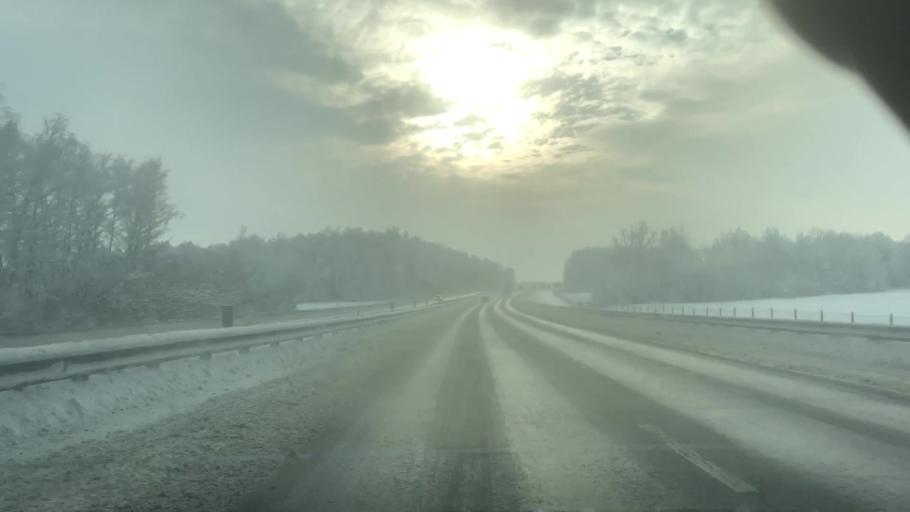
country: RU
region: Tula
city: Venev
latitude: 54.3842
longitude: 38.1544
